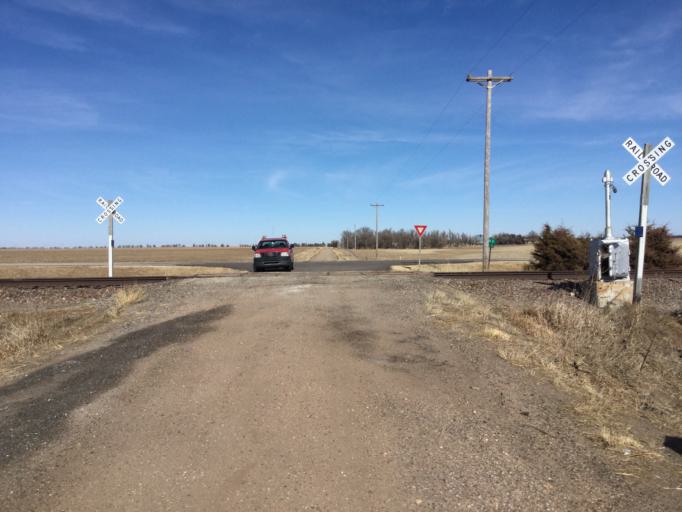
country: US
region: Kansas
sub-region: Rice County
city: Lyons
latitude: 38.5149
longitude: -98.2385
